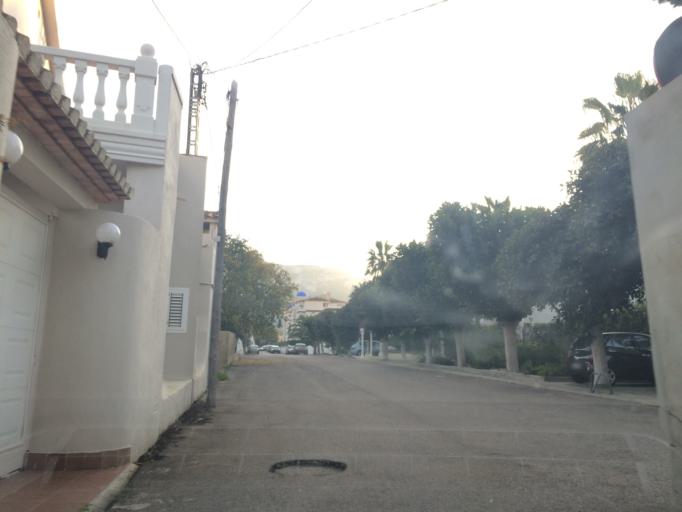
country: ES
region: Valencia
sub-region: Provincia de Alicante
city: Denia
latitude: 38.8335
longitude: 0.1219
